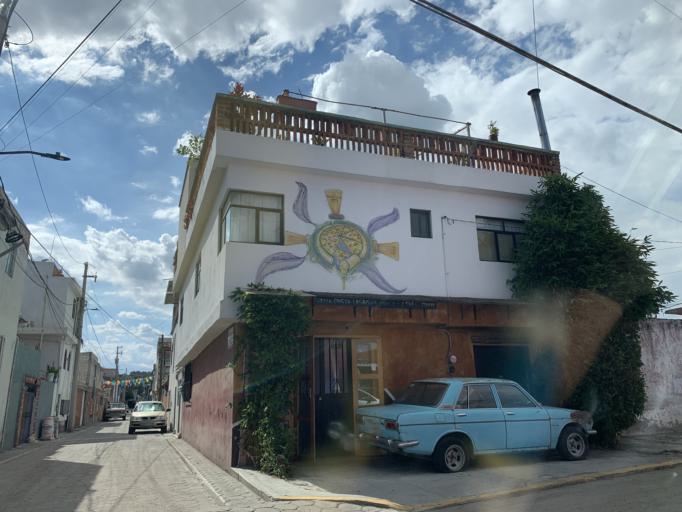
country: MX
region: Puebla
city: Cholula
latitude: 19.0591
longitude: -98.3203
